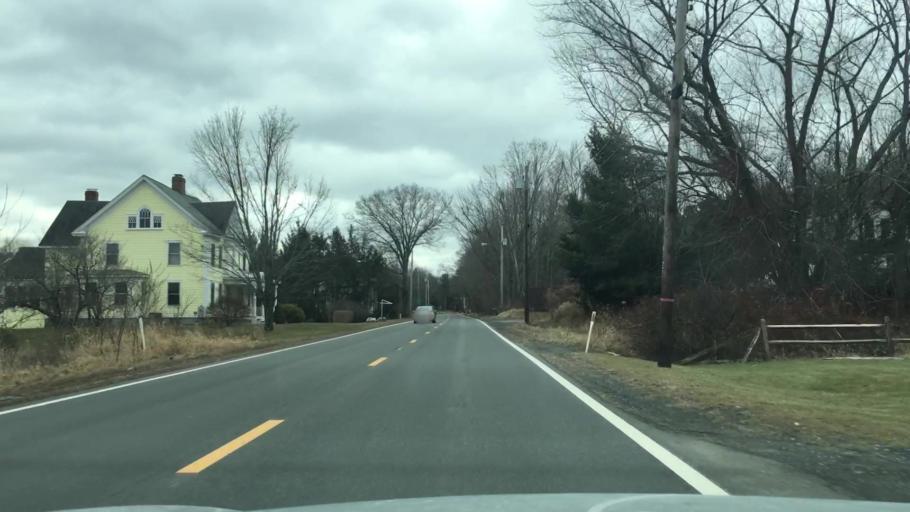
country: US
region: Connecticut
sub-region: Hartford County
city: North Granby
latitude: 42.0044
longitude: -72.7954
